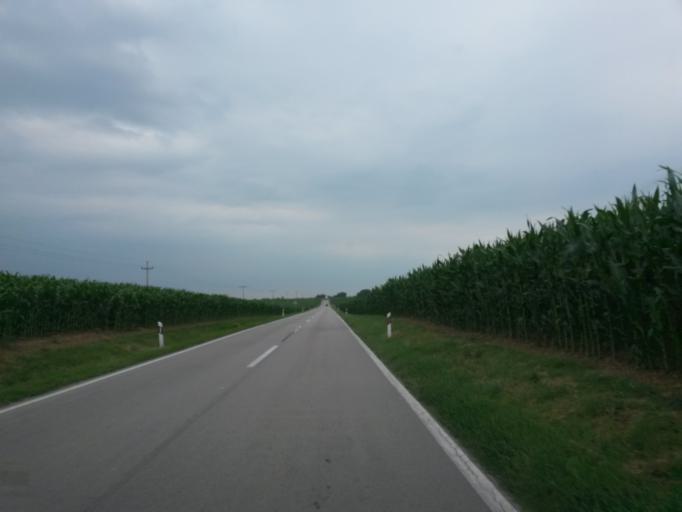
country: HR
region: Vukovarsko-Srijemska
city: Bapska
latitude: 45.2428
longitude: 19.2342
